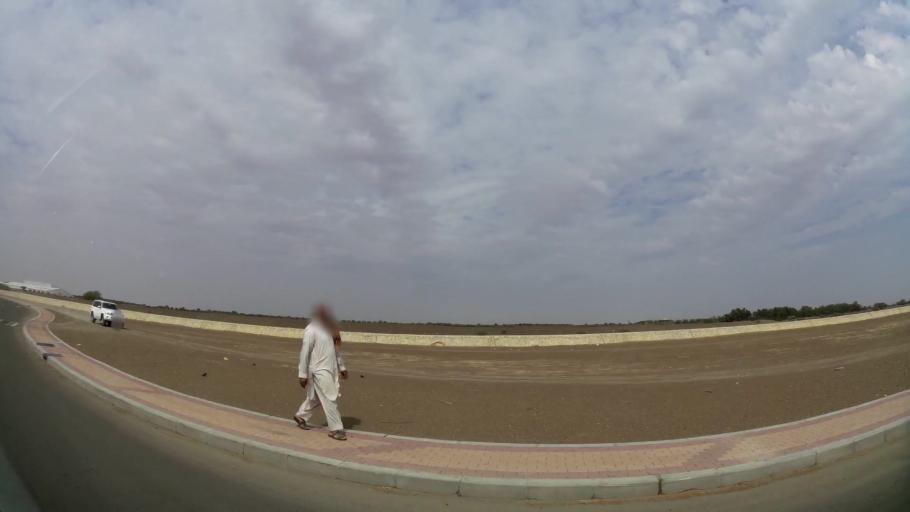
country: AE
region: Abu Dhabi
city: Al Ain
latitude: 24.1957
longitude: 55.8132
